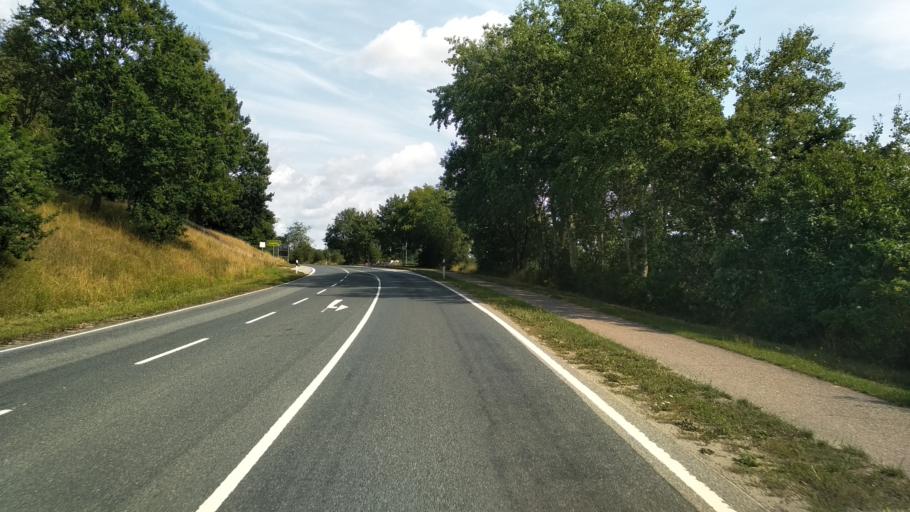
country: DE
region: Schleswig-Holstein
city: Selk
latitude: 54.4767
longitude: 9.5662
